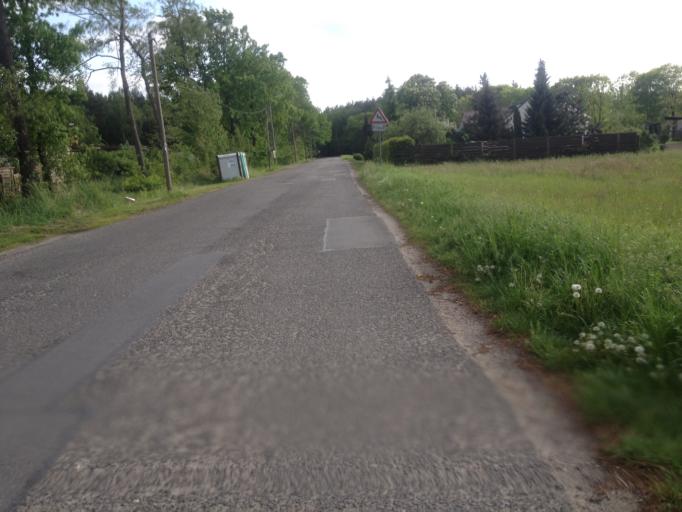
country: DE
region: Brandenburg
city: Cottbus
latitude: 51.8184
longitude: 14.3221
